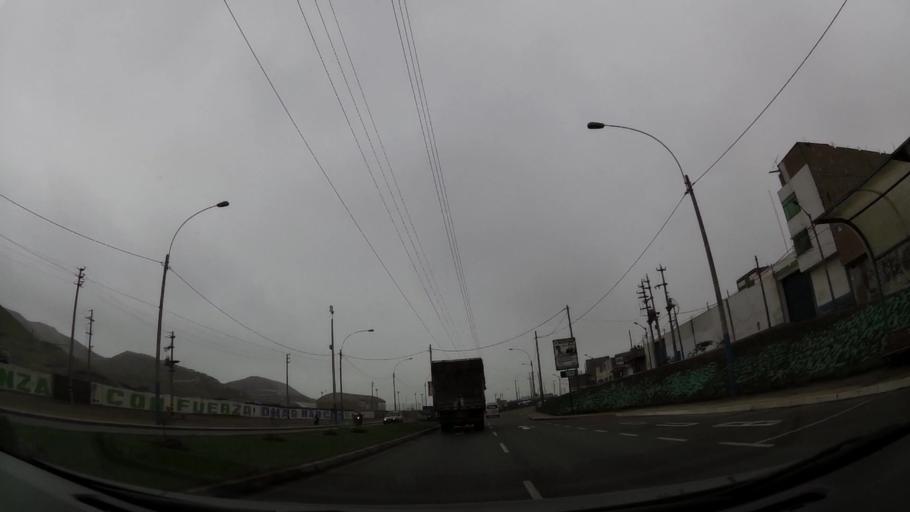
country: PE
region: Lima
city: Ventanilla
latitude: -11.9022
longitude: -77.1283
